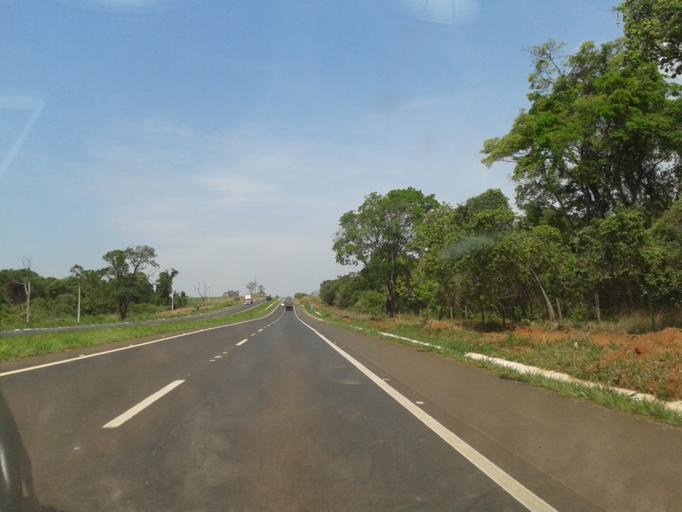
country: BR
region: Minas Gerais
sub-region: Monte Alegre De Minas
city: Monte Alegre de Minas
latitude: -18.8868
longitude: -48.7221
